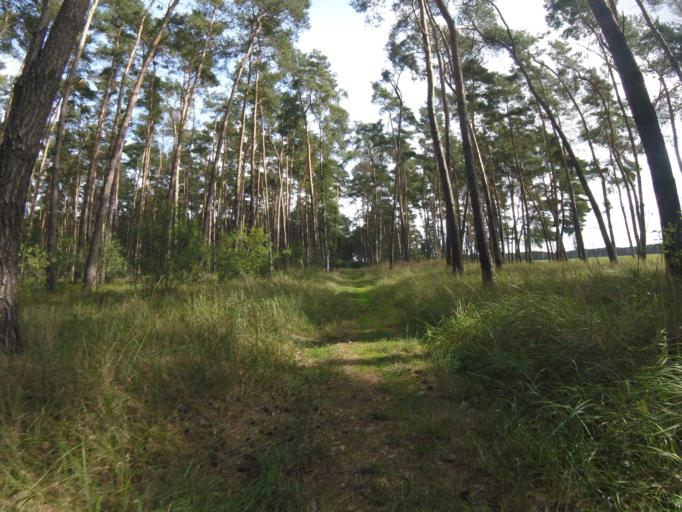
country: DE
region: Brandenburg
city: Mittenwalde
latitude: 52.2311
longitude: 13.5753
